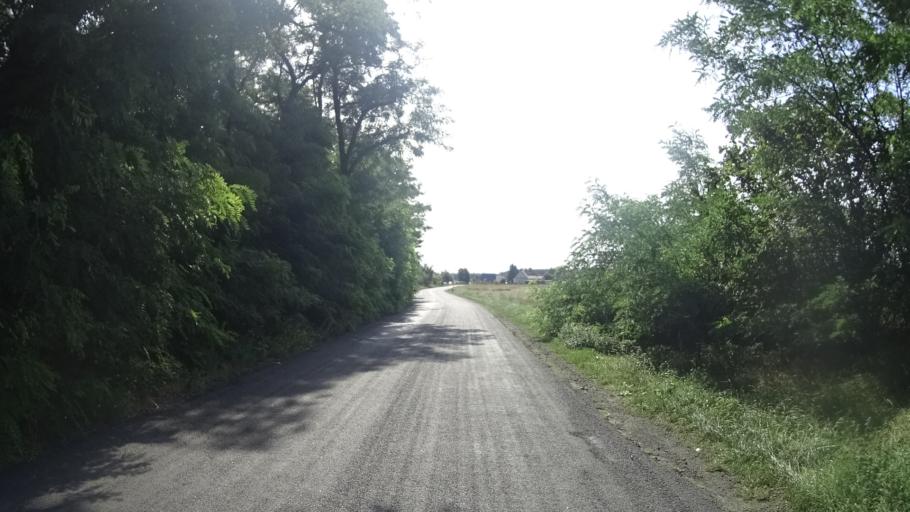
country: DE
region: Brandenburg
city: Golzow
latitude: 52.3121
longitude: 12.6932
